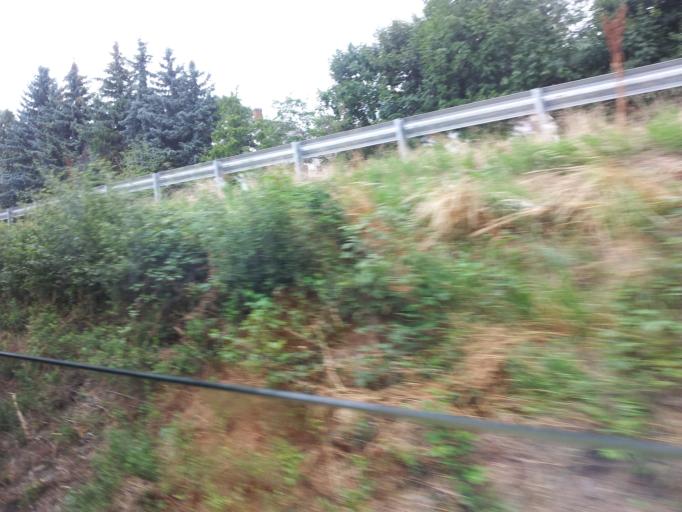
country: HU
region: Veszprem
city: Zanka
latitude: 46.8562
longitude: 17.6685
